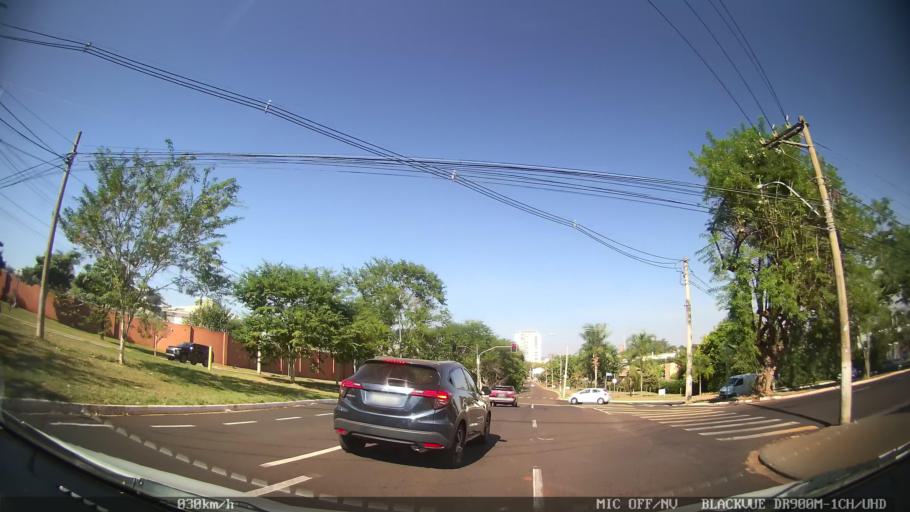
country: BR
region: Sao Paulo
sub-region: Ribeirao Preto
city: Ribeirao Preto
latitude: -21.2197
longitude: -47.8061
